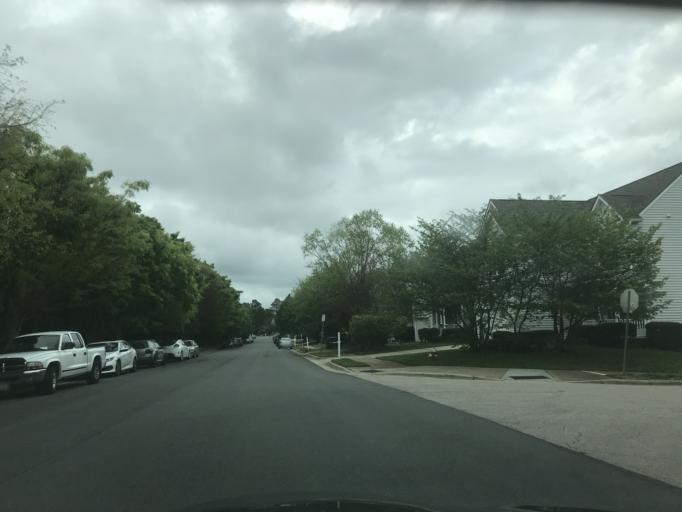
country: US
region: North Carolina
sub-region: Wake County
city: West Raleigh
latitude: 35.7440
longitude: -78.6834
